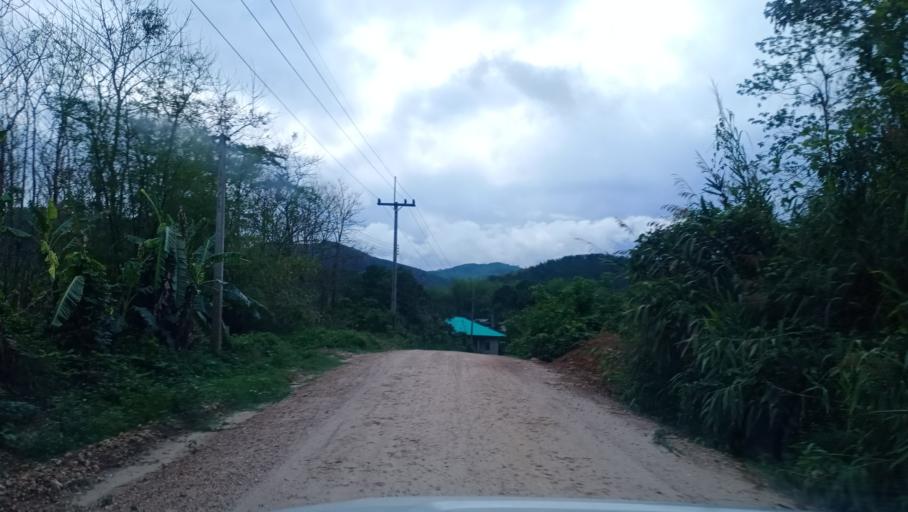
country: LA
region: Phongsali
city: Khoa
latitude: 21.1788
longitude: 102.7103
